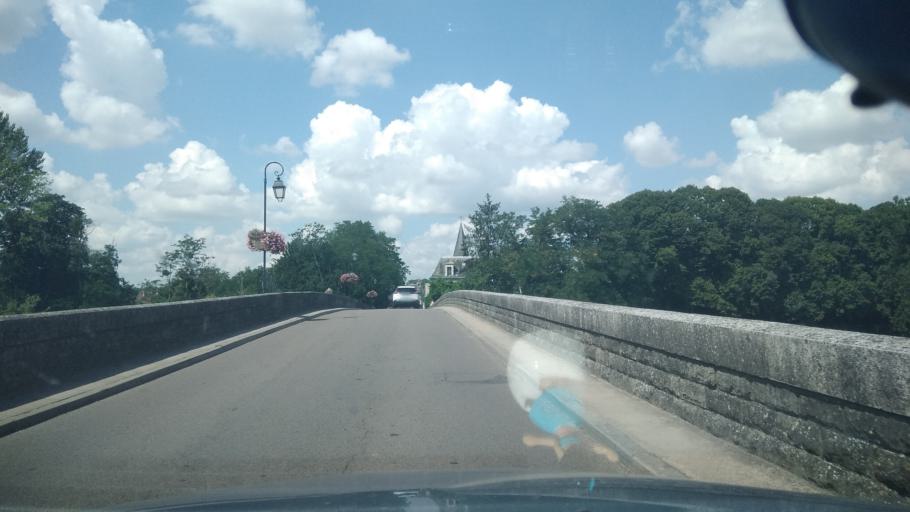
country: FR
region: Poitou-Charentes
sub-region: Departement de la Vienne
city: Dange-Saint-Romain
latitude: 46.9362
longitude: 0.6007
